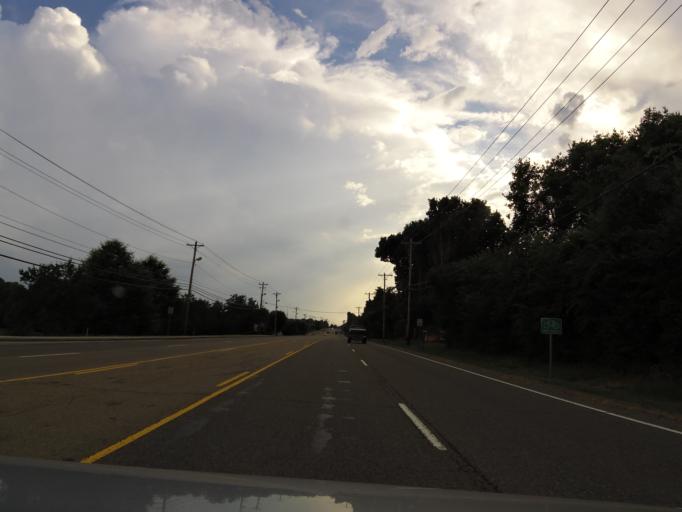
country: US
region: Tennessee
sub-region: Knox County
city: Farragut
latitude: 35.8785
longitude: -84.1665
